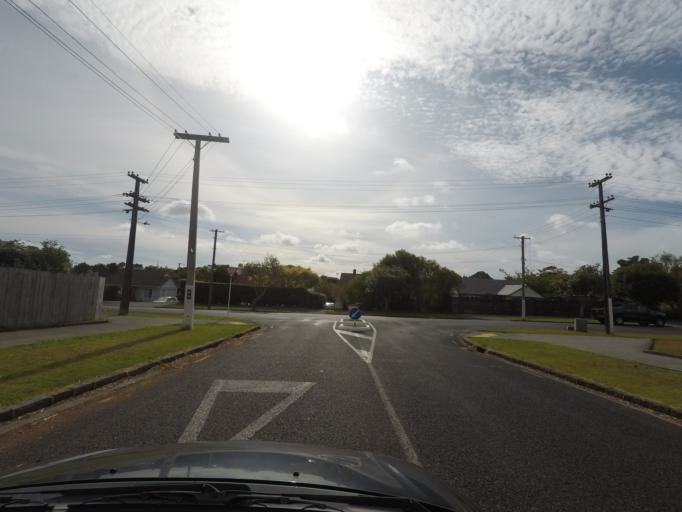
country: NZ
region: Auckland
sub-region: Auckland
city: Rosebank
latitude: -36.8776
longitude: 174.7159
